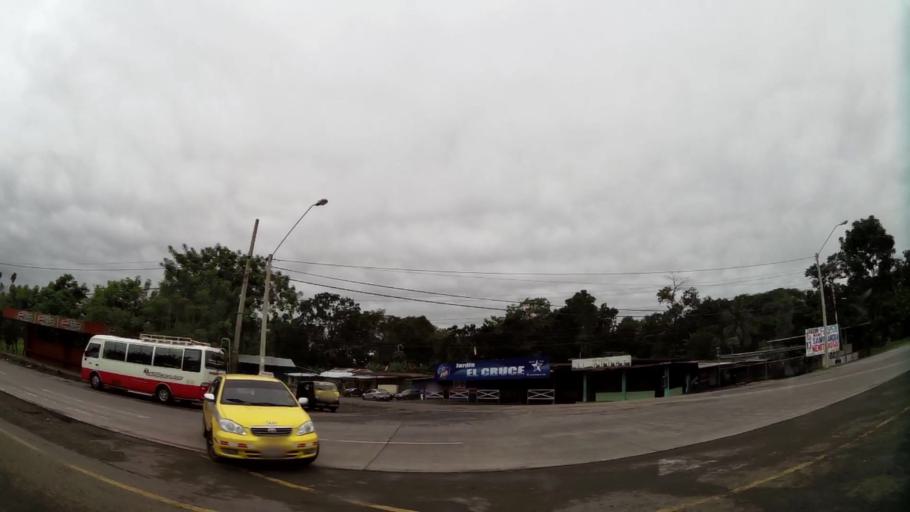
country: PA
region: Chiriqui
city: Tijera
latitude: 8.4816
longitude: -82.5589
